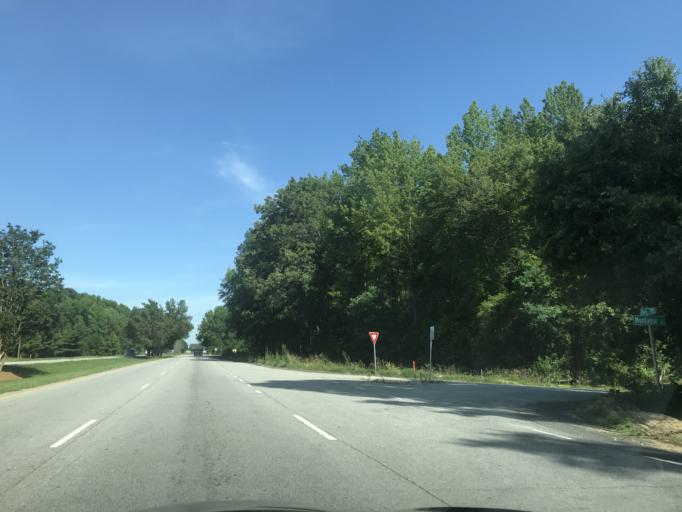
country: US
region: North Carolina
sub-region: Wake County
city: Garner
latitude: 35.7048
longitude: -78.6092
